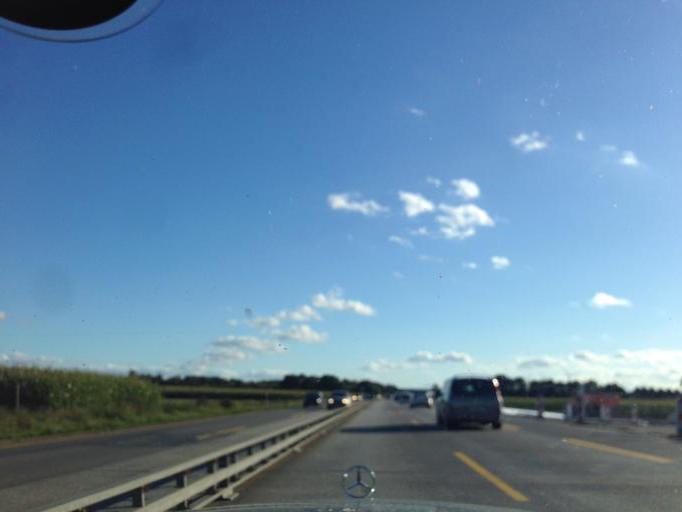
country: DE
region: Schleswig-Holstein
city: Loop
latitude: 54.1516
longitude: 9.9644
